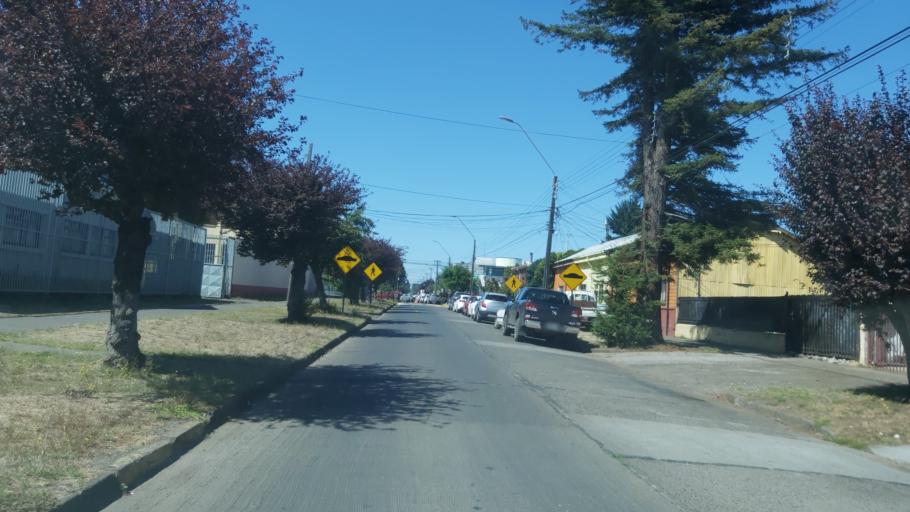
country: CL
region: Araucania
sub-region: Provincia de Malleco
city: Victoria
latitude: -38.2316
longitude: -72.3322
